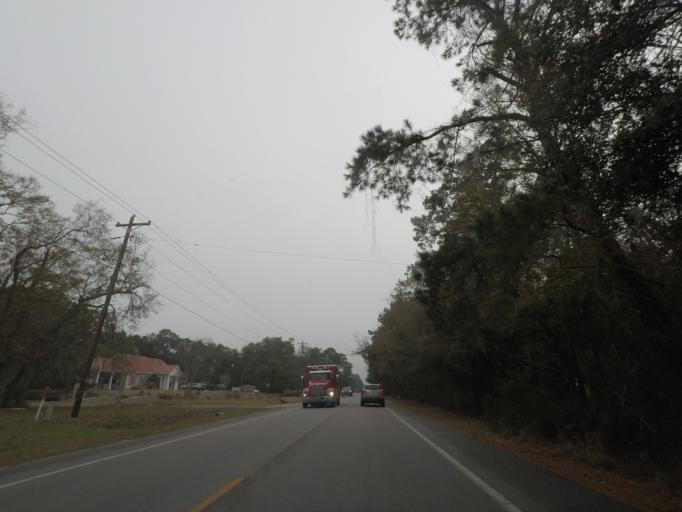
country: US
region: South Carolina
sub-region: Charleston County
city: Seabrook Island
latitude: 32.5194
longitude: -80.2998
